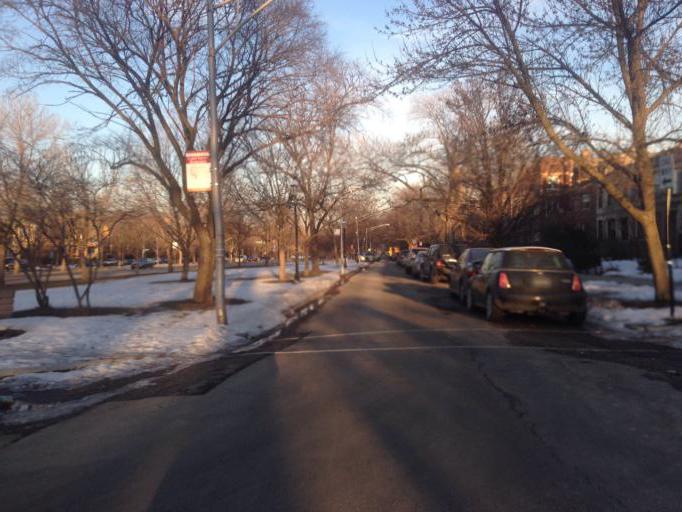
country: US
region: Illinois
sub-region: Cook County
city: Lincolnwood
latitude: 41.9282
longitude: -87.7001
